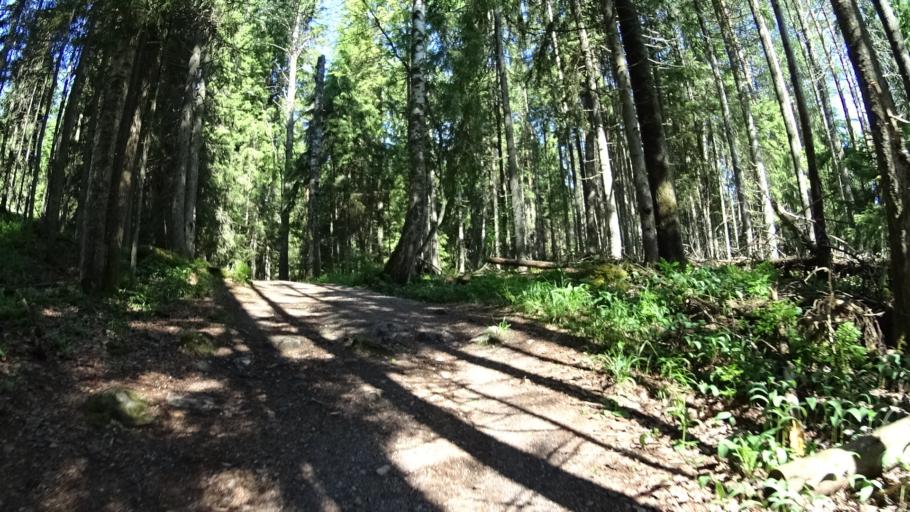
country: FI
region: Uusimaa
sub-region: Helsinki
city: Espoo
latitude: 60.3380
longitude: 24.6747
